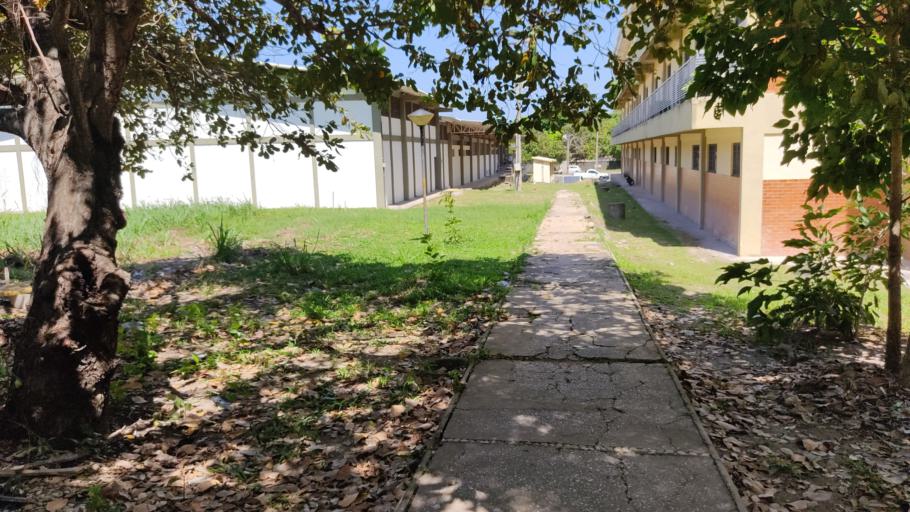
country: BR
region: Piaui
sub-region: Teresina
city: Teresina
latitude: -5.0564
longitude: -42.7921
